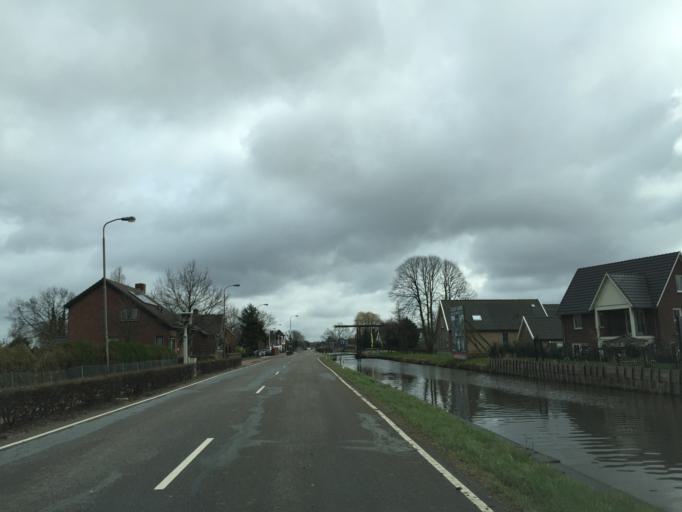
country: NL
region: South Holland
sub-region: Gemeente Lansingerland
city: Berkel en Rodenrijs
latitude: 52.0261
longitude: 4.4810
